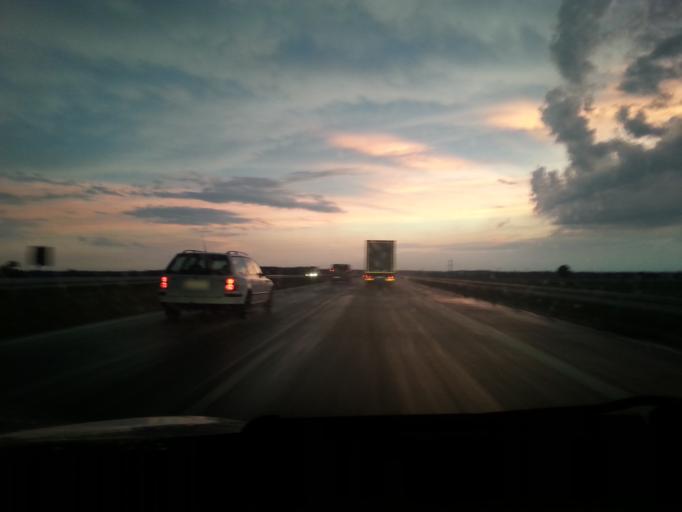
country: PL
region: Lodz Voivodeship
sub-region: Powiat laski
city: Lask
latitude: 51.5543
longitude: 19.0759
